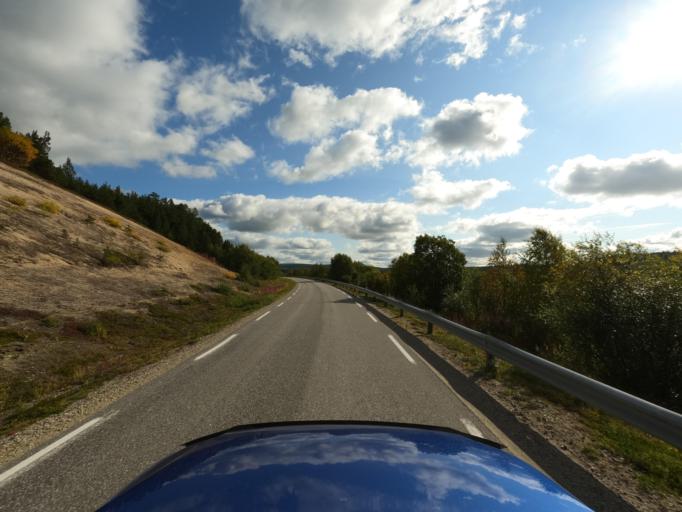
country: NO
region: Finnmark Fylke
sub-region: Karasjok
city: Karasjohka
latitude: 69.4442
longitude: 25.2153
